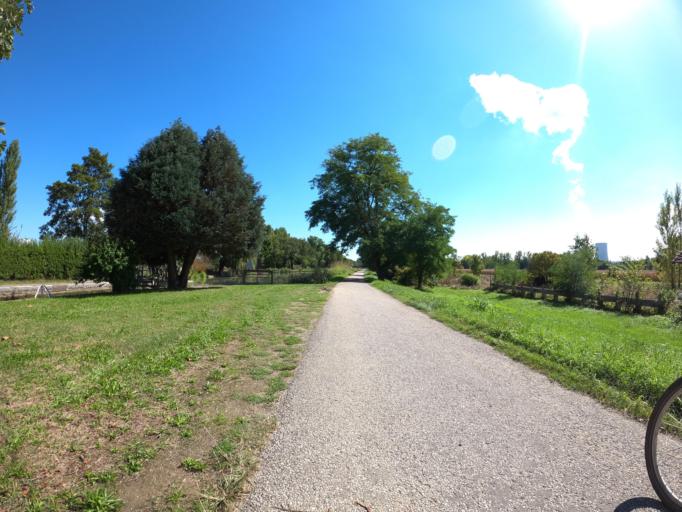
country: FR
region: Midi-Pyrenees
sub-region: Departement du Tarn-et-Garonne
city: Lamagistere
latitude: 44.1281
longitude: 0.8338
